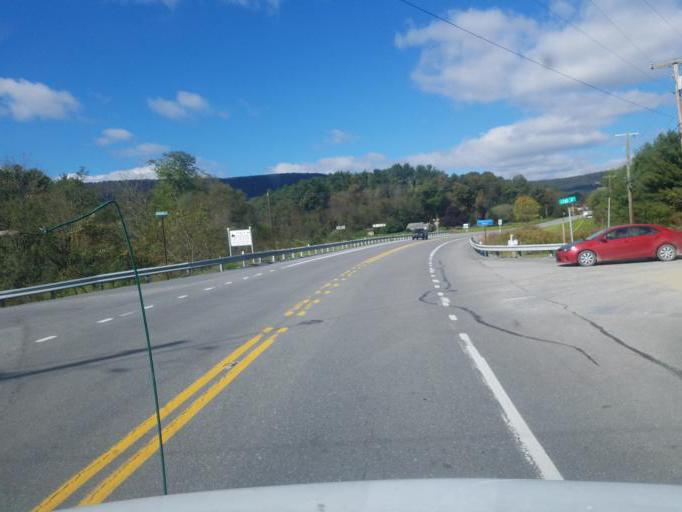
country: US
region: Pennsylvania
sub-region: Fulton County
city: McConnellsburg
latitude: 39.9977
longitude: -78.0972
